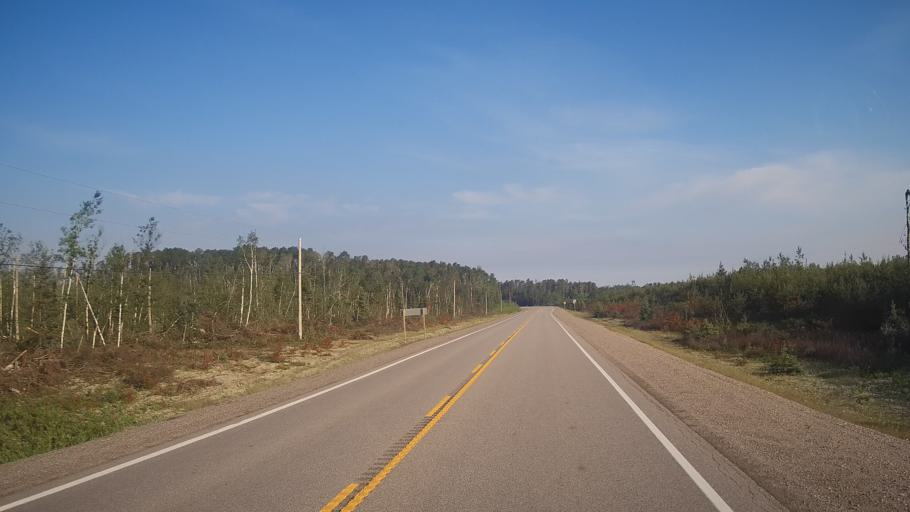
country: CA
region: Ontario
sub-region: Rainy River District
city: Atikokan
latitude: 49.3667
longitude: -91.5544
